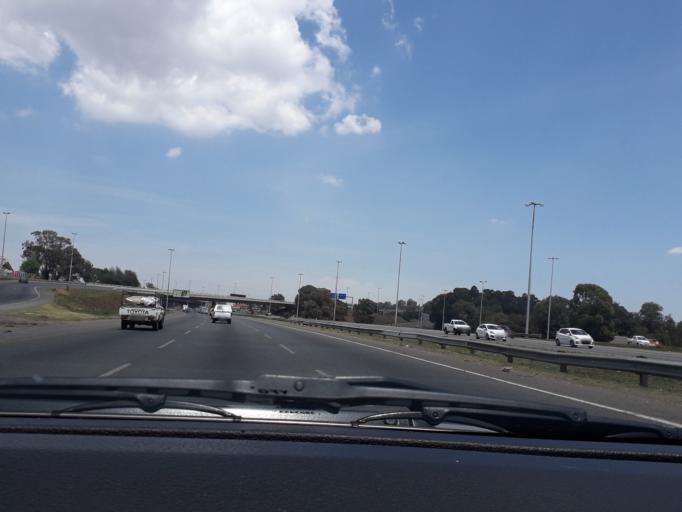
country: ZA
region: Gauteng
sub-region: City of Johannesburg Metropolitan Municipality
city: Johannesburg
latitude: -26.2543
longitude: 27.9922
